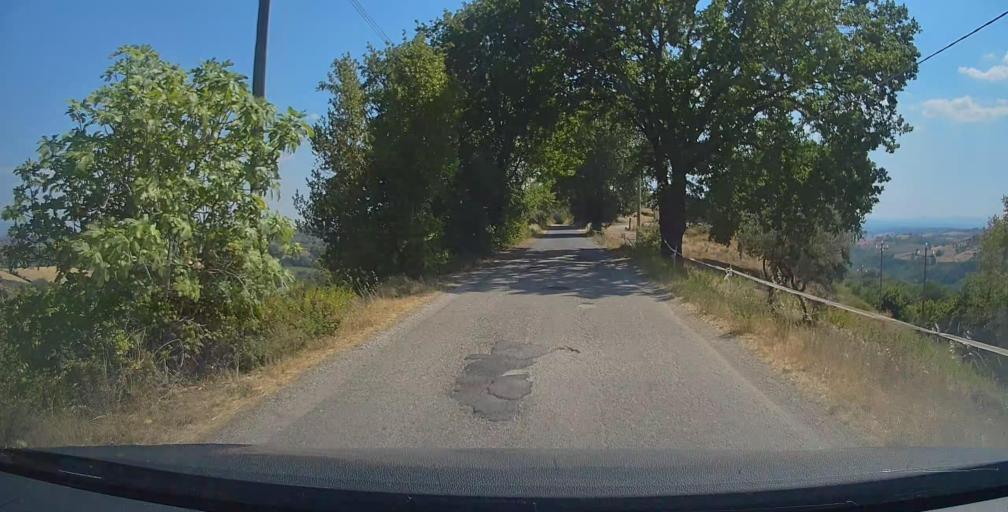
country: IT
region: Umbria
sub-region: Provincia di Terni
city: Calvi dell'Umbria
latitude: 42.3805
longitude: 12.5687
